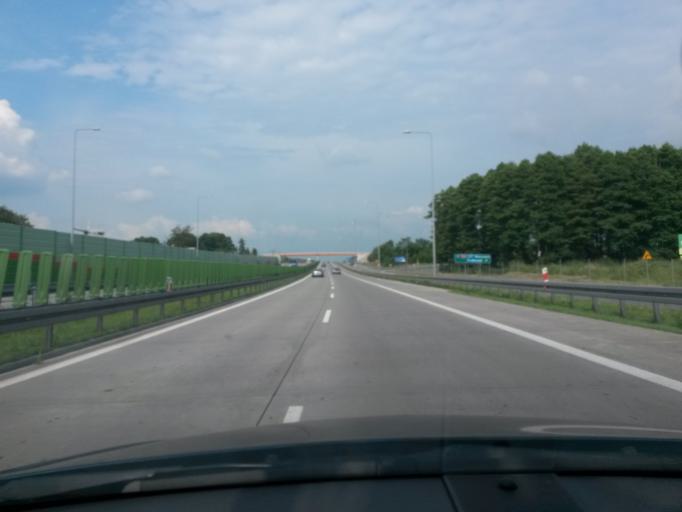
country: PL
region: Lodz Voivodeship
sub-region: Powiat piotrkowski
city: Wolborz
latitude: 51.5074
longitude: 19.8909
